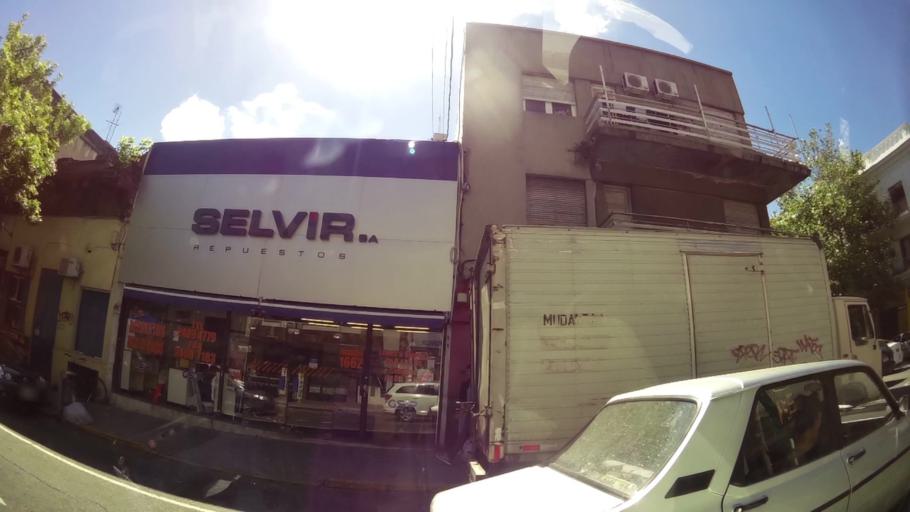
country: UY
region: Montevideo
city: Montevideo
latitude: -34.8999
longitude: -56.1886
